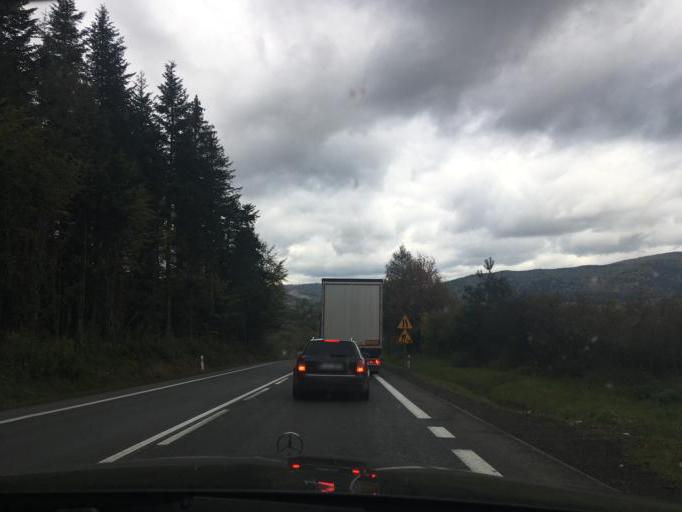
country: PL
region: Subcarpathian Voivodeship
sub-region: Powiat krosnienski
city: Dukla
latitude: 49.4914
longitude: 21.7038
